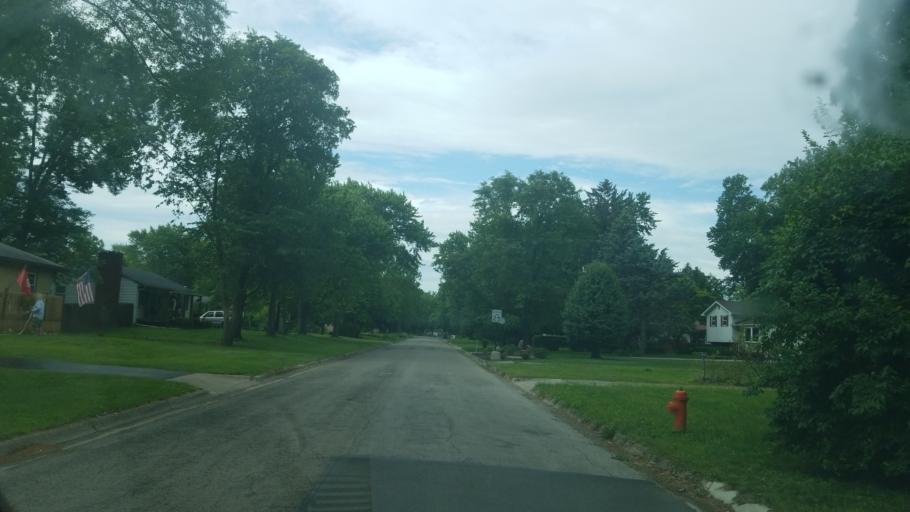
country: US
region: Ohio
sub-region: Franklin County
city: Worthington
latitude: 40.0574
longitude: -82.9962
